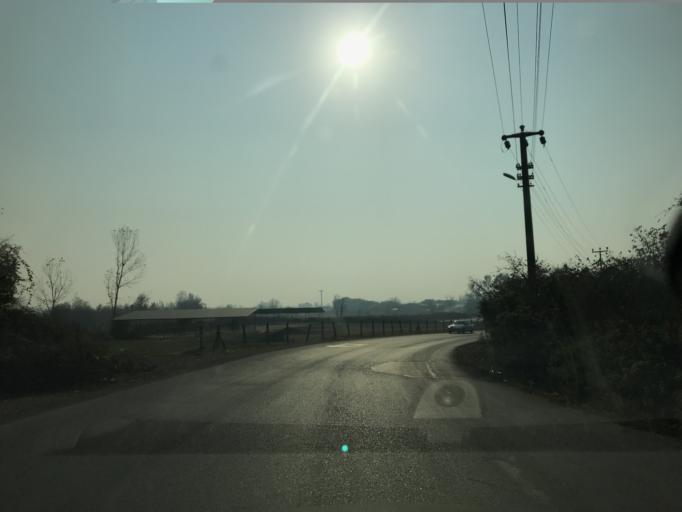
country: TR
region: Duzce
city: Cumayeri
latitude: 40.8882
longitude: 30.9519
